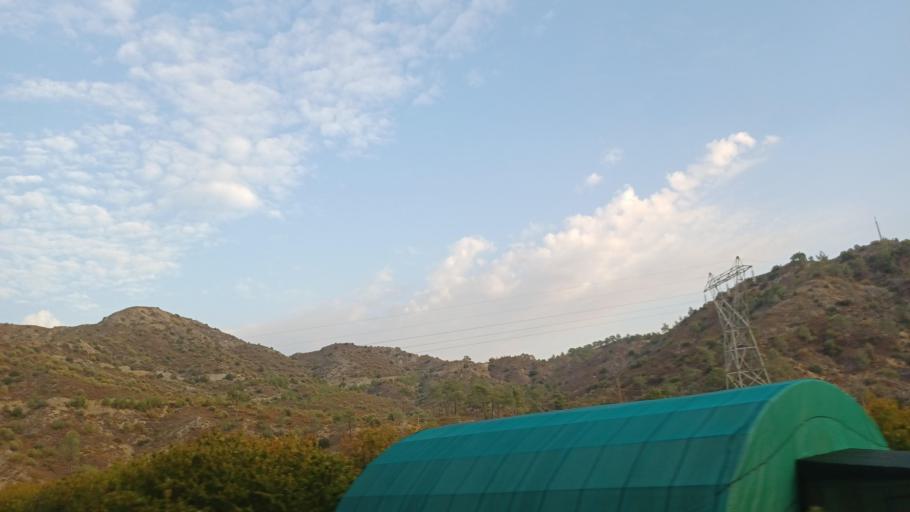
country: CY
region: Limassol
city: Pelendri
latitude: 34.8703
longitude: 32.9180
